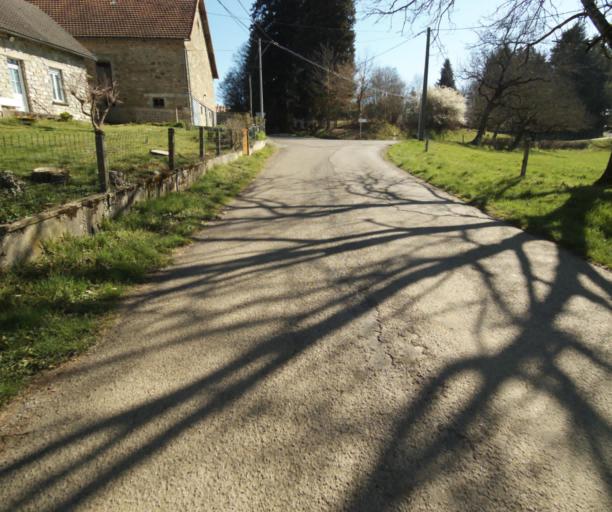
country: FR
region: Limousin
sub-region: Departement de la Correze
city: Seilhac
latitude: 45.3723
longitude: 1.7399
